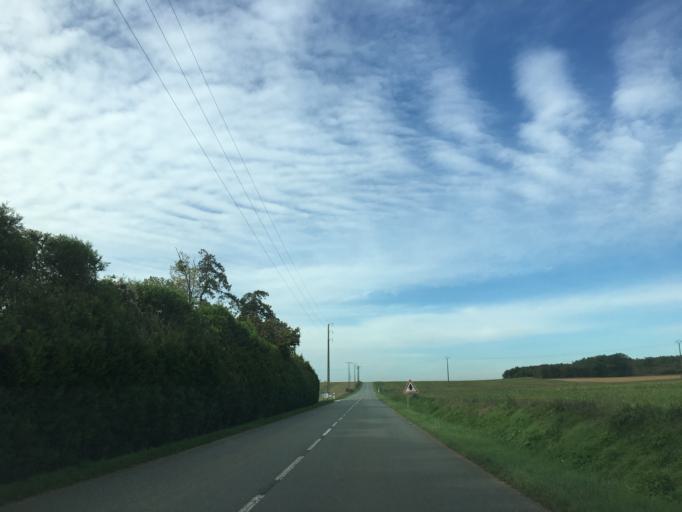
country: FR
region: Poitou-Charentes
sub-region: Departement de la Charente-Maritime
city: Aulnay
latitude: 46.0699
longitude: -0.4389
